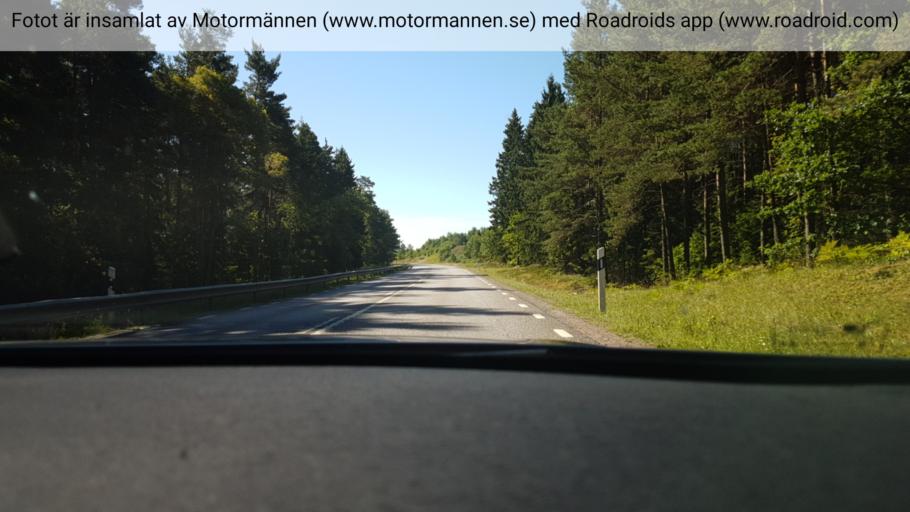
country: SE
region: Vaestra Goetaland
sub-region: Skovde Kommun
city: Skultorp
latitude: 58.2461
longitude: 13.8171
